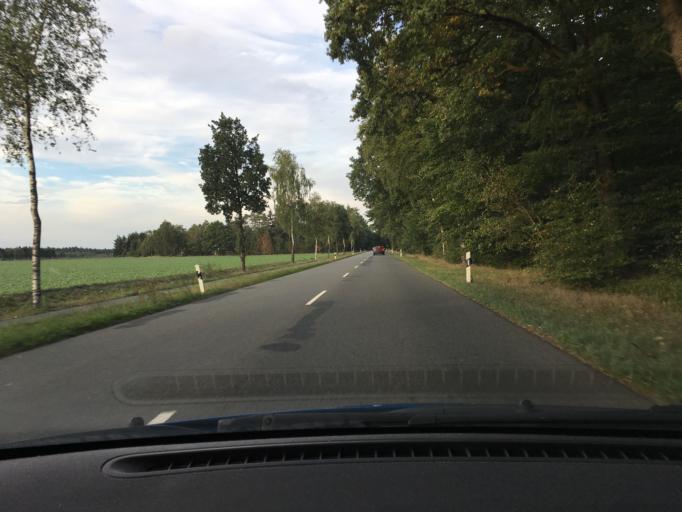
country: DE
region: Lower Saxony
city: Bispingen
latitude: 53.0523
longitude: 9.9451
